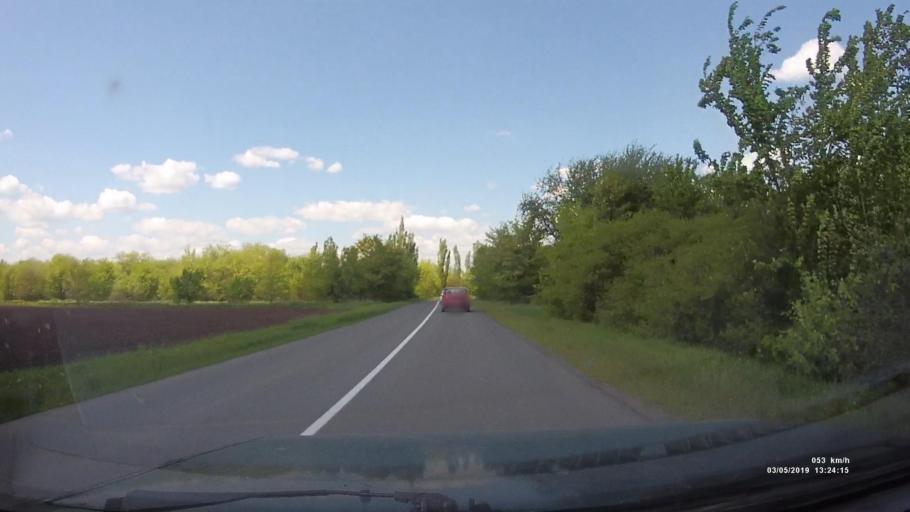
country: RU
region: Rostov
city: Semikarakorsk
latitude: 47.5636
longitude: 40.7957
